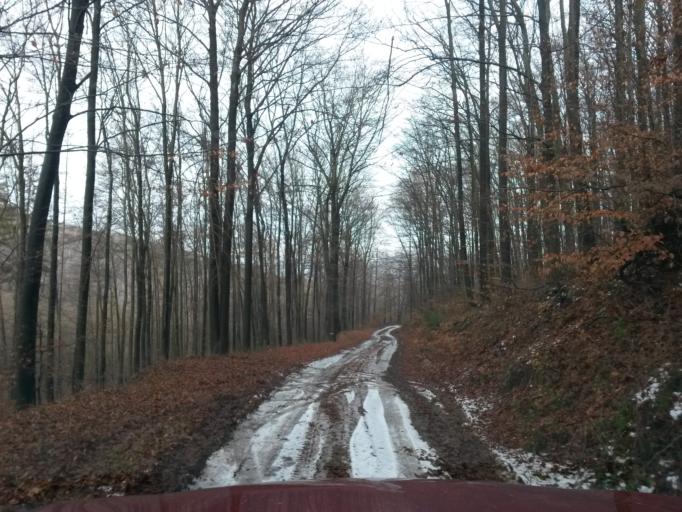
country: SK
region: Kosicky
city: Dobsina
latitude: 48.7478
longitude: 20.3941
